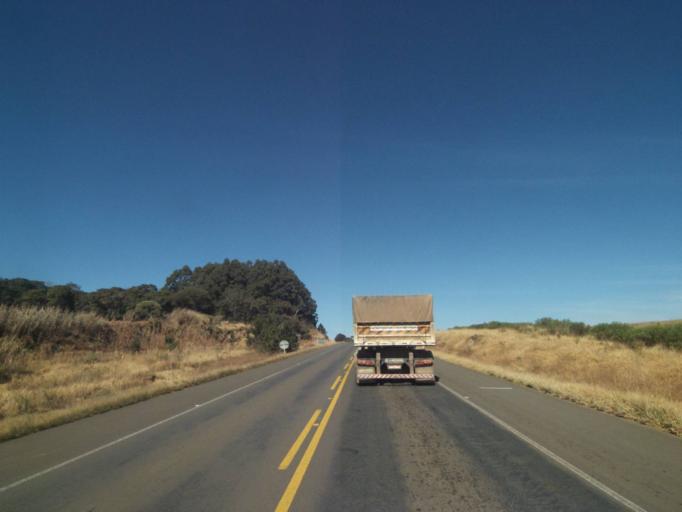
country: BR
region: Parana
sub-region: Tibagi
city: Tibagi
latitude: -24.7607
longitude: -50.4701
